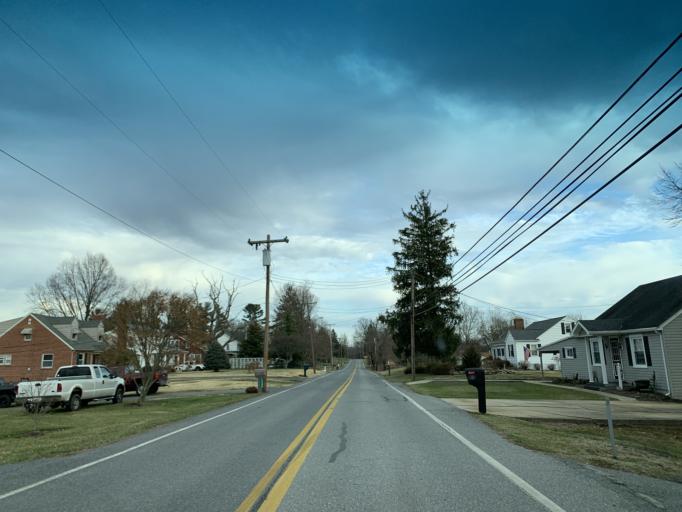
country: US
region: Maryland
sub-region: Frederick County
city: Brunswick
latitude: 39.3306
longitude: -77.6263
